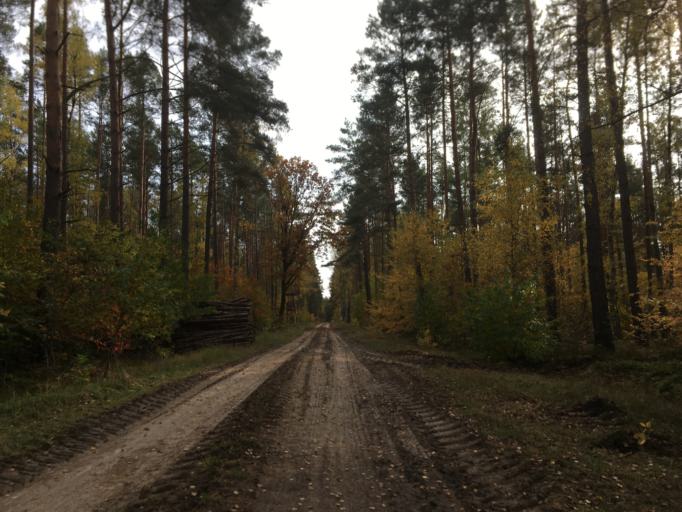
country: DE
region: Brandenburg
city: Liebenwalde
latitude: 52.9412
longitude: 13.4991
